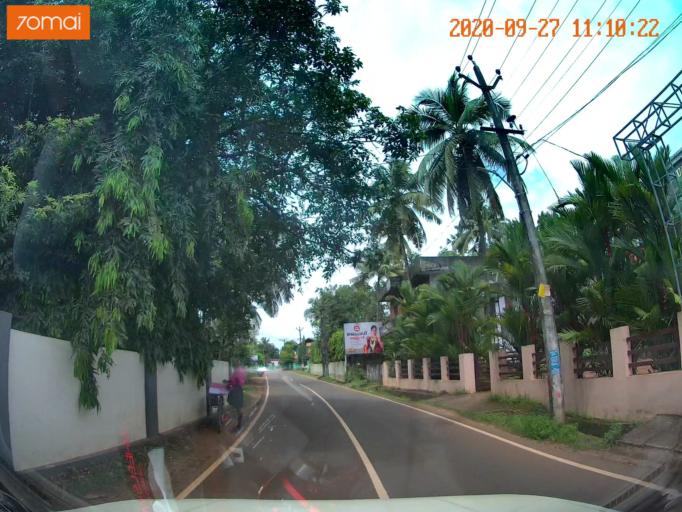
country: IN
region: Kerala
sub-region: Thrissur District
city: Trichur
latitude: 10.4305
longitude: 76.2205
